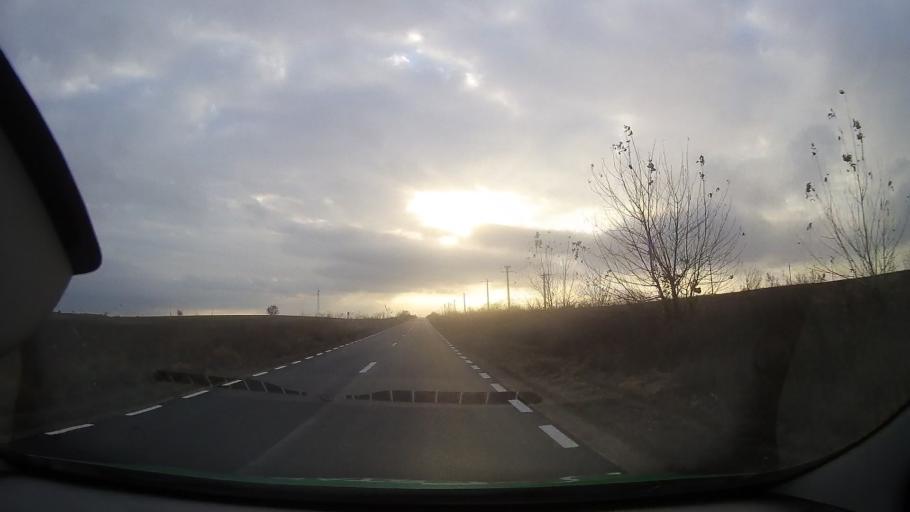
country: RO
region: Constanta
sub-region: Comuna Adamclisi
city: Adamclisi
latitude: 44.0722
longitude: 27.9844
